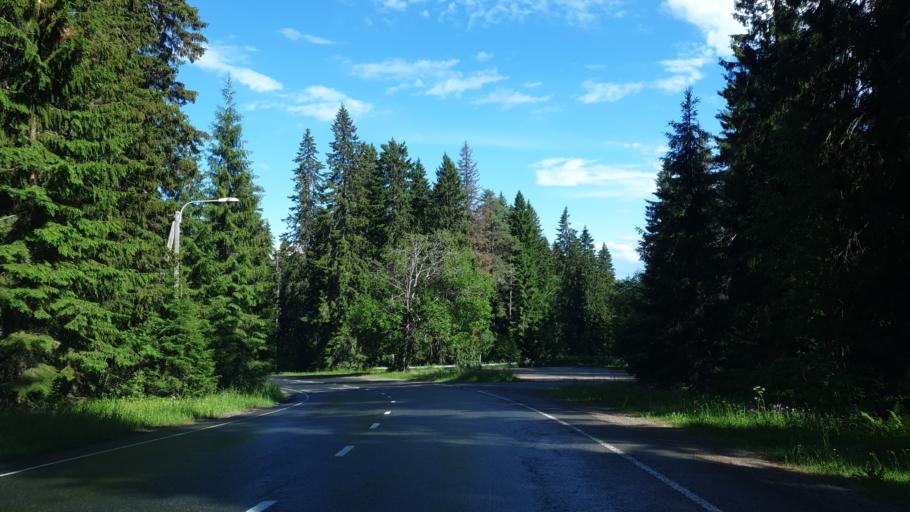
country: FI
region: Northern Savo
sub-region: Kuopio
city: Kuopio
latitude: 62.9090
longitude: 27.6577
